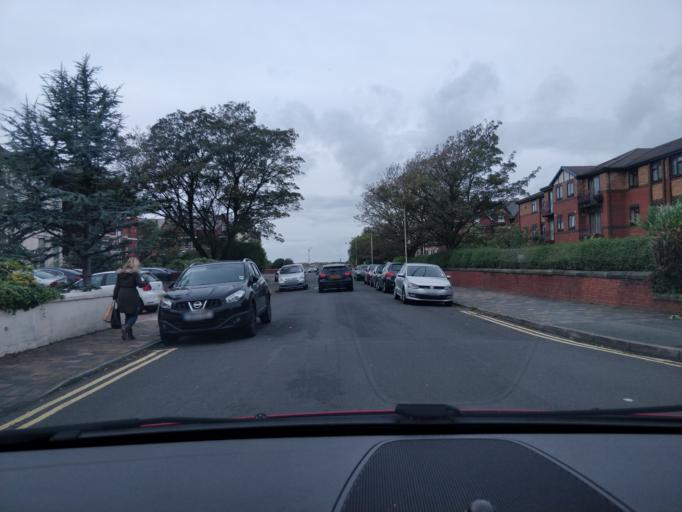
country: GB
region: England
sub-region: Sefton
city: Southport
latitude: 53.6549
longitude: -2.9996
